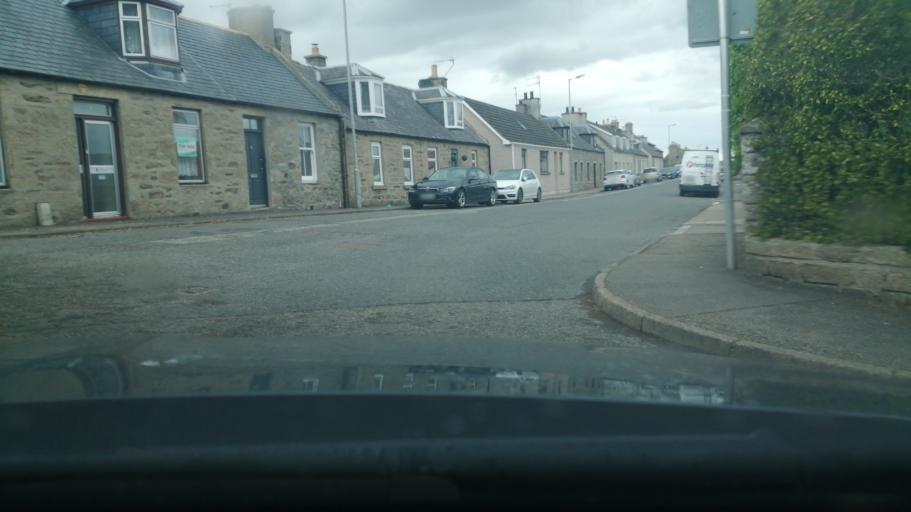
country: GB
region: Scotland
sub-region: Moray
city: Keith
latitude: 57.5363
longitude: -2.9528
